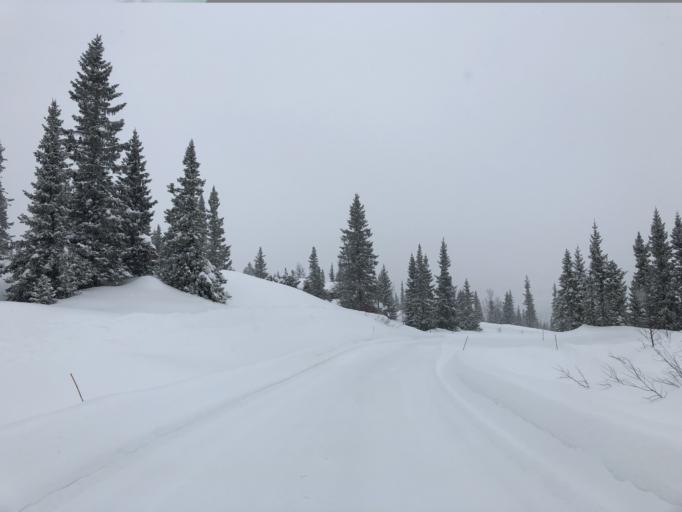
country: NO
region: Oppland
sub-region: Gausdal
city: Segalstad bru
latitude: 61.3269
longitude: 10.0550
